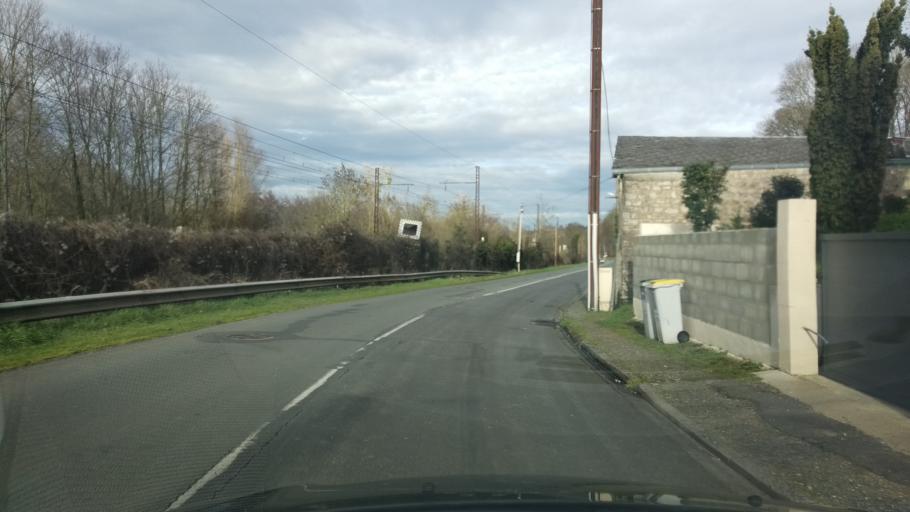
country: FR
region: Poitou-Charentes
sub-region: Departement de la Vienne
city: Poitiers
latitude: 46.6012
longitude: 0.3443
